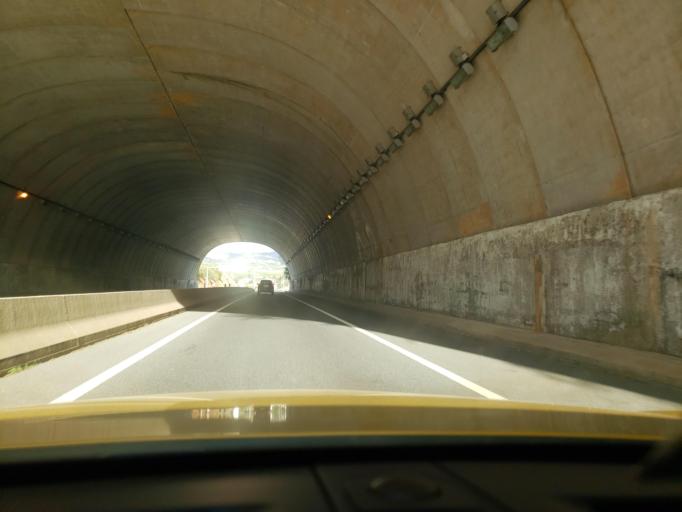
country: PT
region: Faro
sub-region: Silves
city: Silves
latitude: 37.1796
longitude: -8.4425
